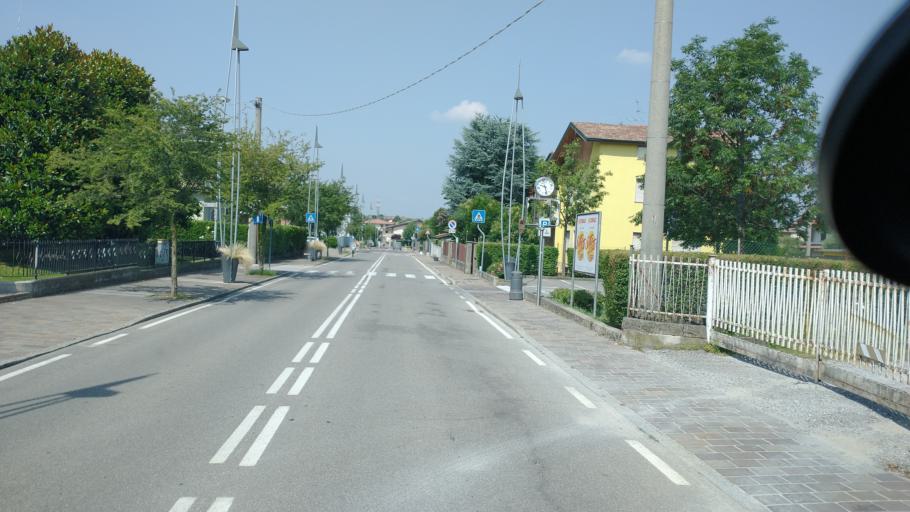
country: IT
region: Lombardy
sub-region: Provincia di Bergamo
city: Levate
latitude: 45.6268
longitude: 9.6244
